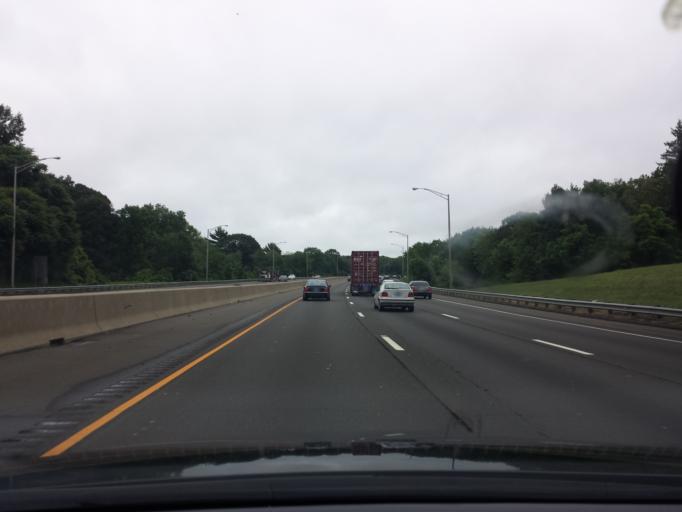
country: US
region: Connecticut
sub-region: New Haven County
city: City of Milford (balance)
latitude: 41.2372
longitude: -73.0599
